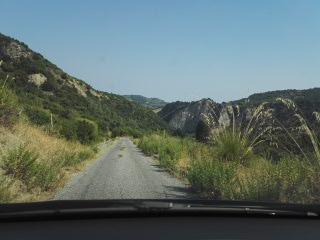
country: IT
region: Calabria
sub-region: Provincia di Reggio Calabria
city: Camini
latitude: 38.4439
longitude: 16.4717
